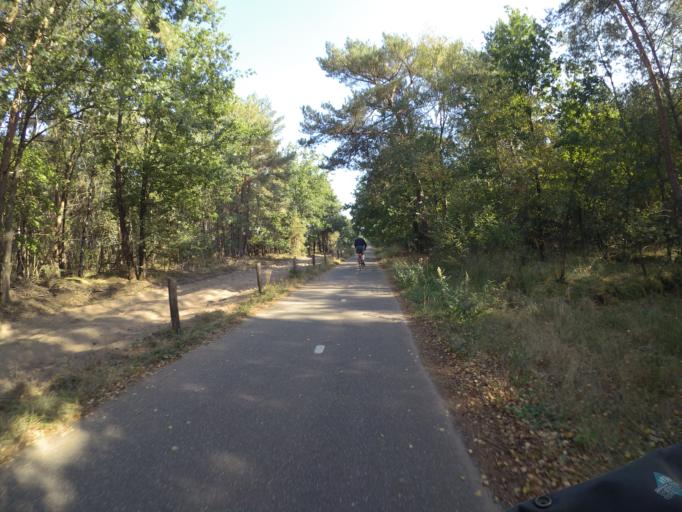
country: NL
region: North Brabant
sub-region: Gemeente Oirschot
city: Oirschot
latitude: 51.4652
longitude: 5.3095
